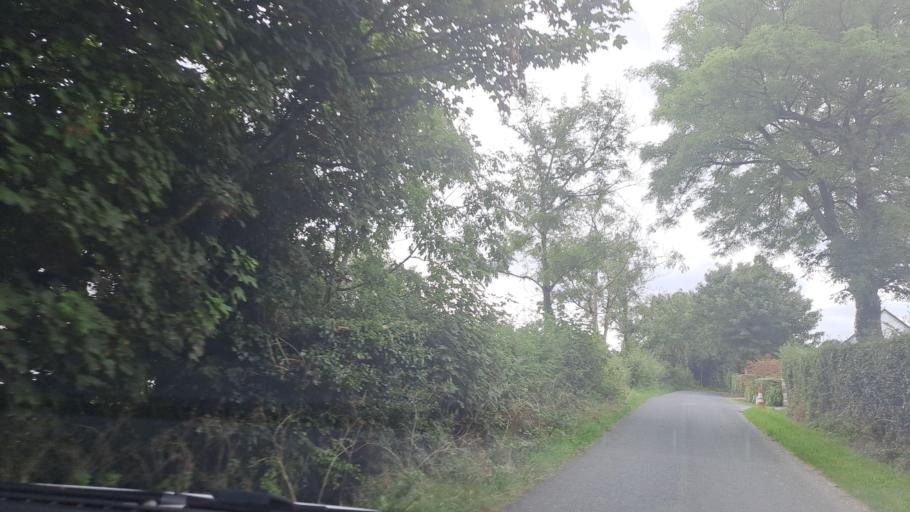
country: IE
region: Ulster
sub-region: An Cabhan
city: Kingscourt
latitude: 53.9678
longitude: -6.8518
